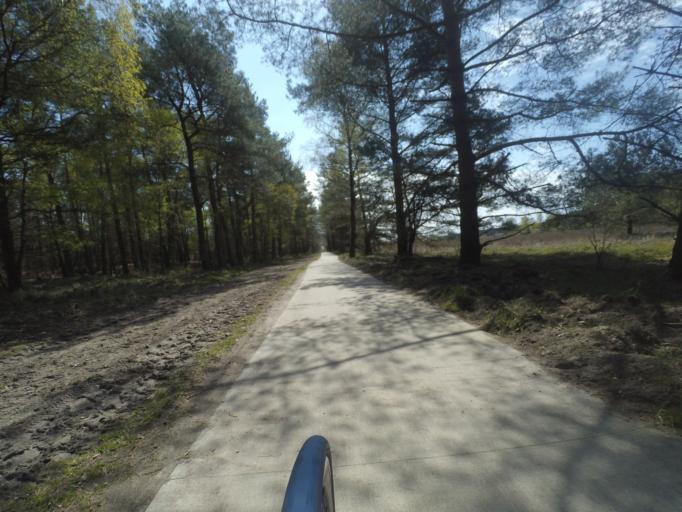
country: NL
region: Gelderland
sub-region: Gemeente Epe
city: Emst
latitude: 52.3323
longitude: 5.8833
